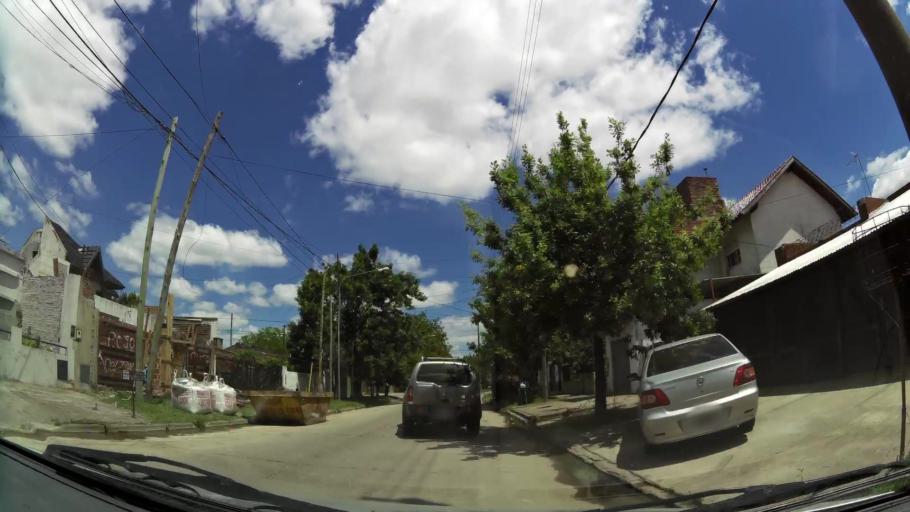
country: AR
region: Buenos Aires
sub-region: Partido de Lanus
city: Lanus
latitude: -34.7058
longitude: -58.4214
